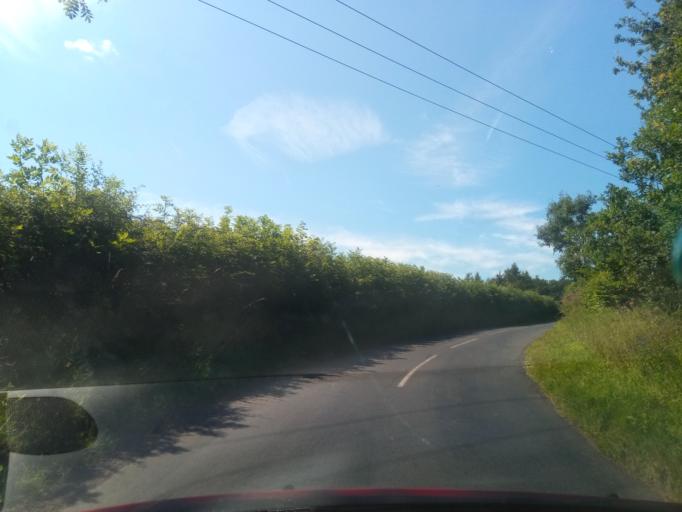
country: GB
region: England
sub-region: Northumberland
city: Wall
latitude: 54.9996
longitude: -2.1972
